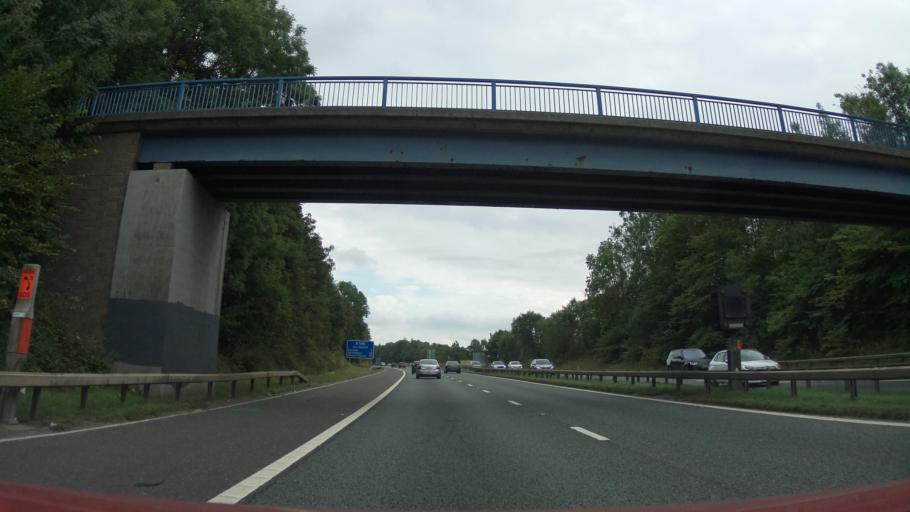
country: GB
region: England
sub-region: County Durham
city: Chester-le-Street
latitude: 54.8593
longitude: -1.5556
